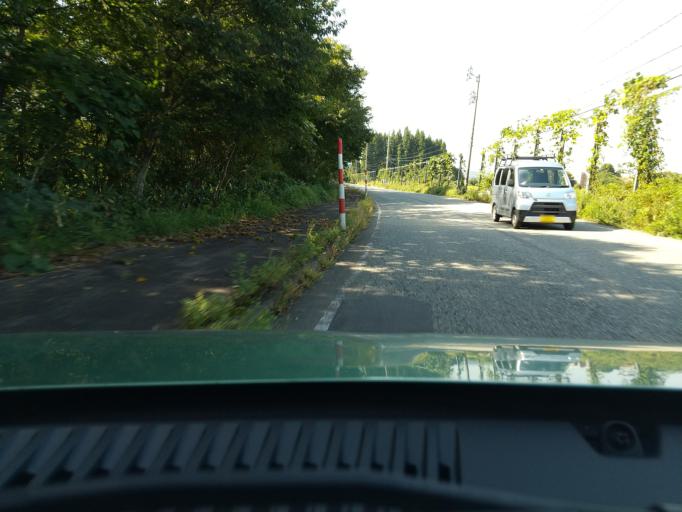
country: JP
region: Akita
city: Akita
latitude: 39.5972
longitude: 140.3050
